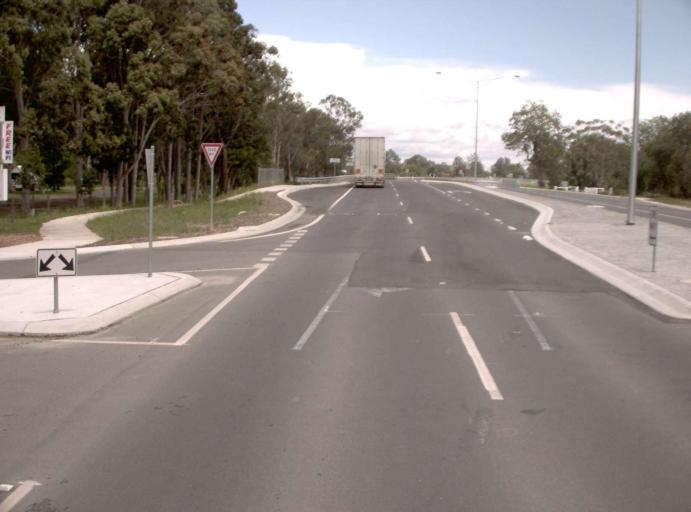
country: AU
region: Victoria
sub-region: Wellington
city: Sale
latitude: -38.1122
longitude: 147.0570
